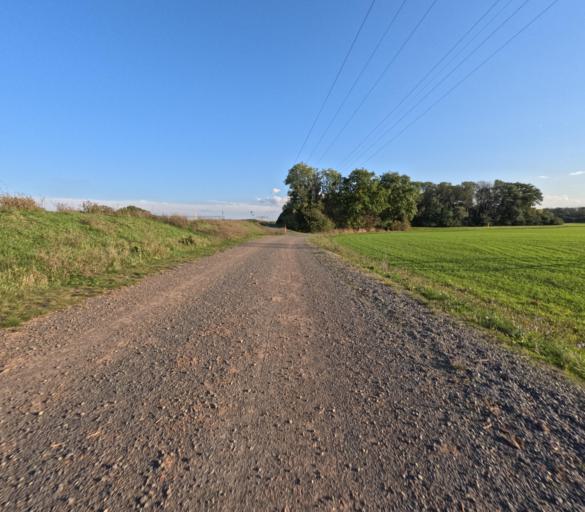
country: DE
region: Saxony
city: Schkeuditz
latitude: 51.3761
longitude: 12.2767
